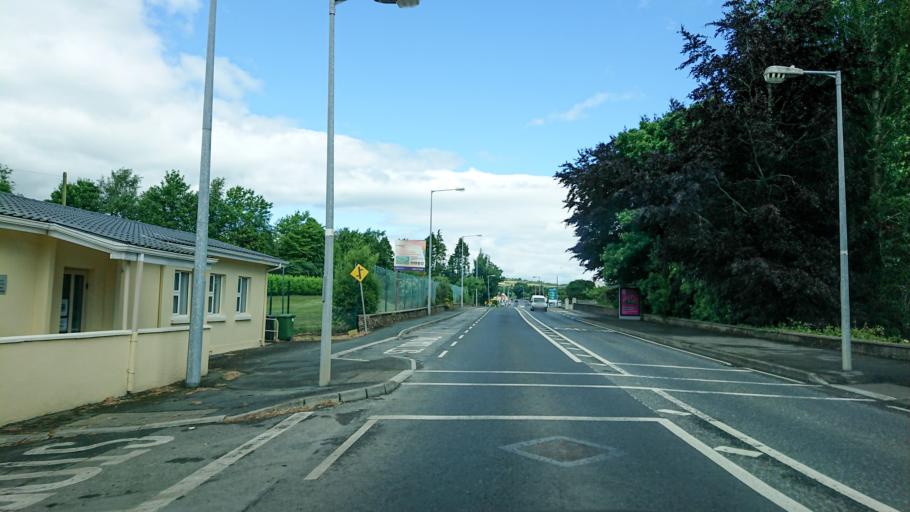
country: IE
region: Leinster
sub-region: Kilkenny
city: Mooncoin
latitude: 52.2318
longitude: -7.2409
